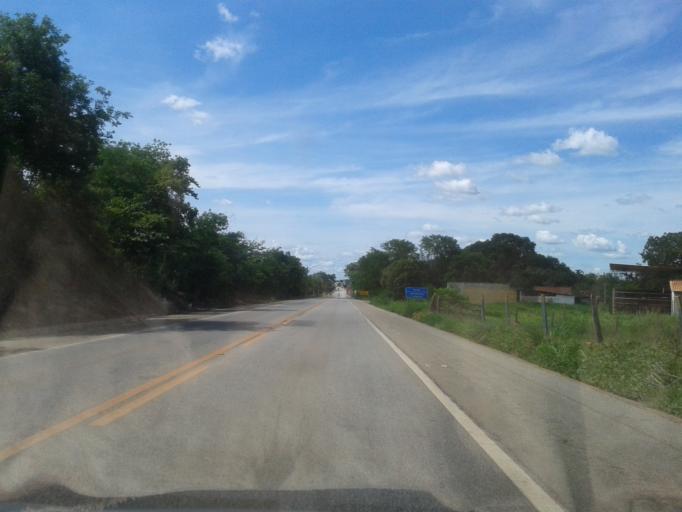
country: BR
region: Goias
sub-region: Itapuranga
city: Itapuranga
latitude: -15.4589
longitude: -50.3573
